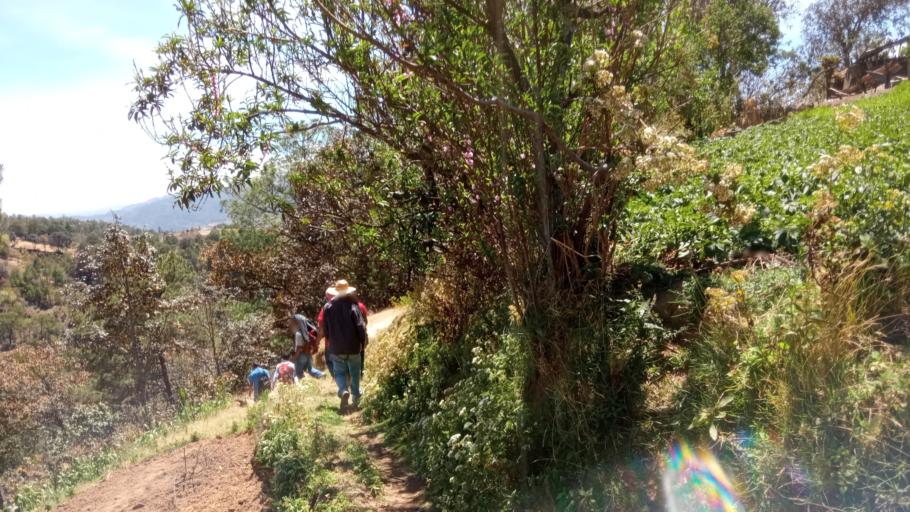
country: GT
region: San Marcos
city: Tejutla
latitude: 15.1291
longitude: -91.7928
